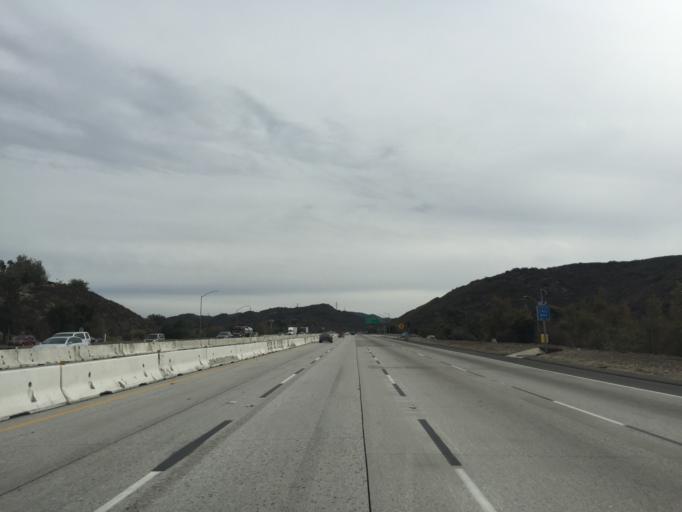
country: US
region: California
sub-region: Los Angeles County
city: Burbank
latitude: 34.2618
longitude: -118.3320
